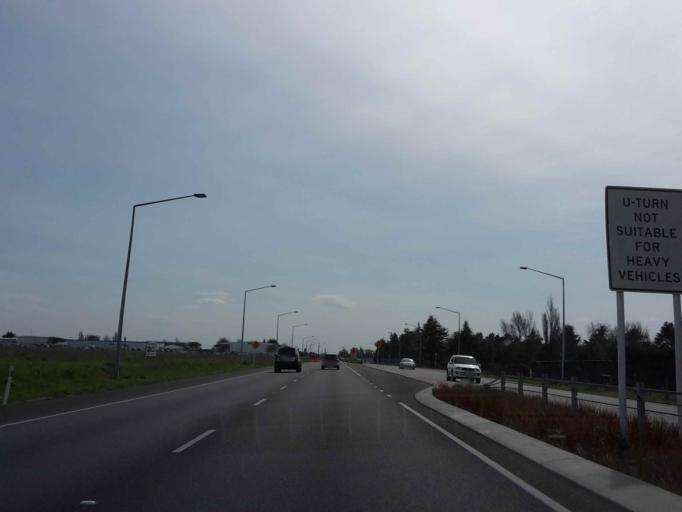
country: NZ
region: Canterbury
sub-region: Selwyn District
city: Prebbleton
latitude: -43.5010
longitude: 172.5453
